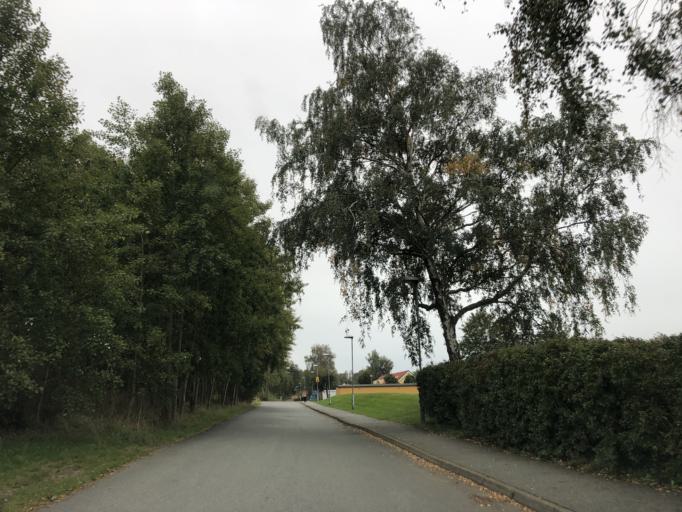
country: SE
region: Vaestra Goetaland
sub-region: Goteborg
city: Majorna
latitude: 57.6544
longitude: 11.8813
